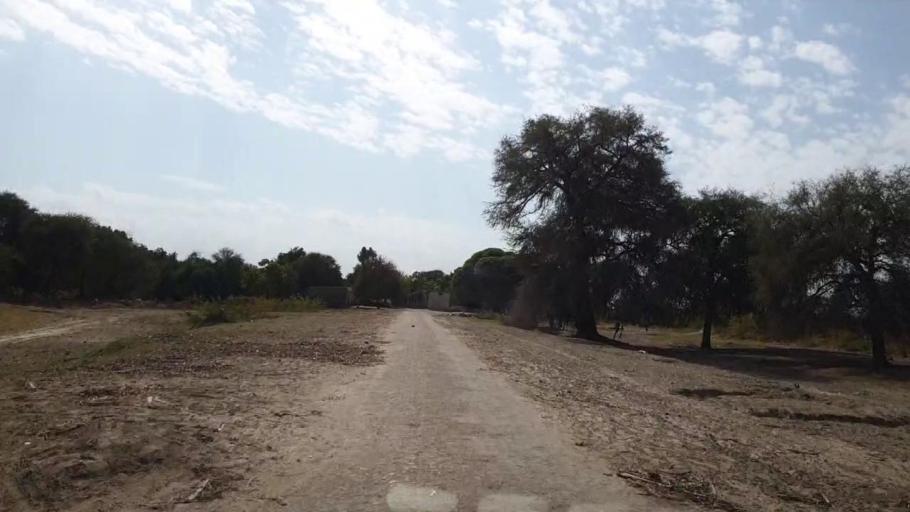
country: PK
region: Sindh
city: Matiari
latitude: 25.5445
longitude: 68.5459
